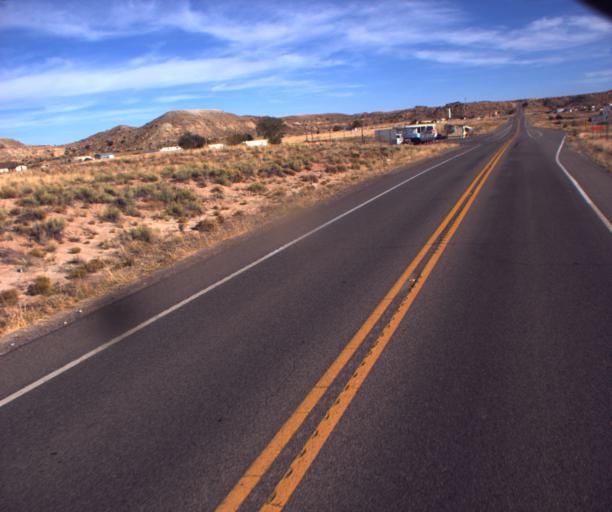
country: US
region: New Mexico
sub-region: San Juan County
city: Shiprock
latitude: 36.9237
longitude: -109.0924
